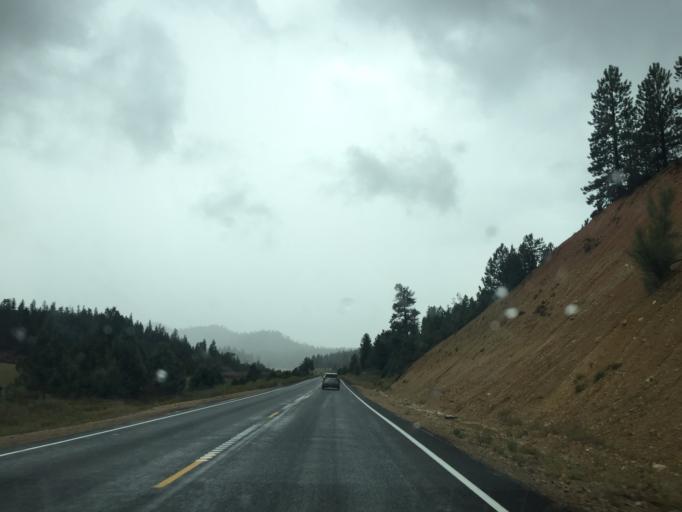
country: US
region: Utah
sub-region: Kane County
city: Kanab
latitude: 37.4367
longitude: -112.5383
